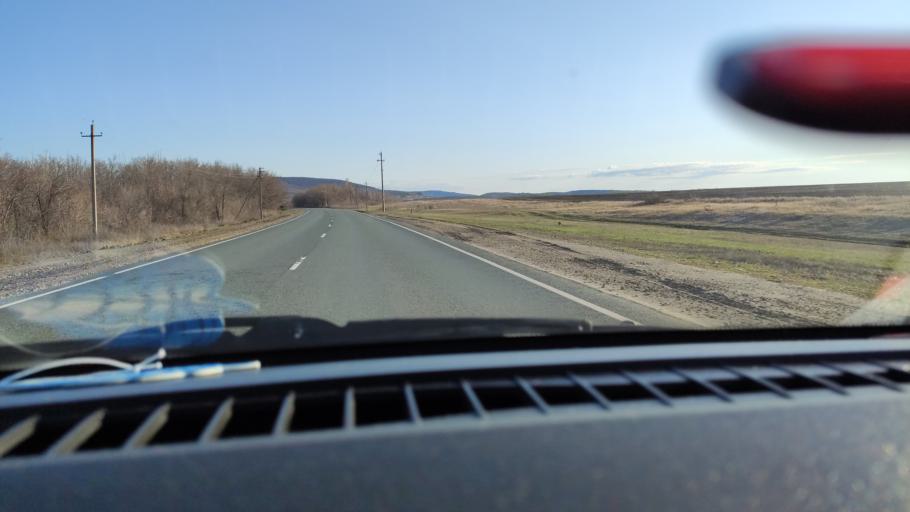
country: RU
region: Saratov
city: Alekseyevka
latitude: 52.2708
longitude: 47.9288
